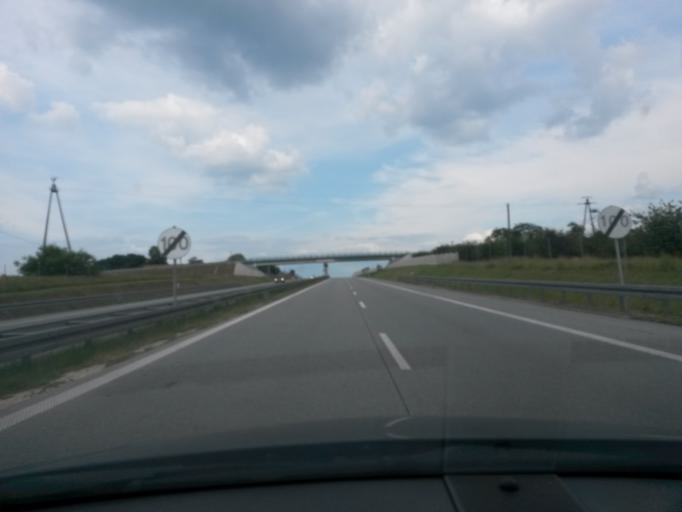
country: PL
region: Lodz Voivodeship
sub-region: Powiat skierniewicki
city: Kowiesy
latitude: 51.8787
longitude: 20.3943
